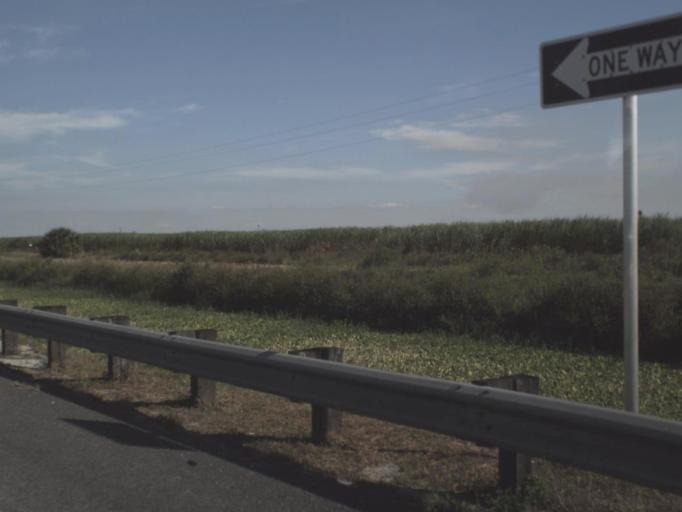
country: US
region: Florida
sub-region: Hendry County
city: Harlem
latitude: 26.7540
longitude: -80.9996
